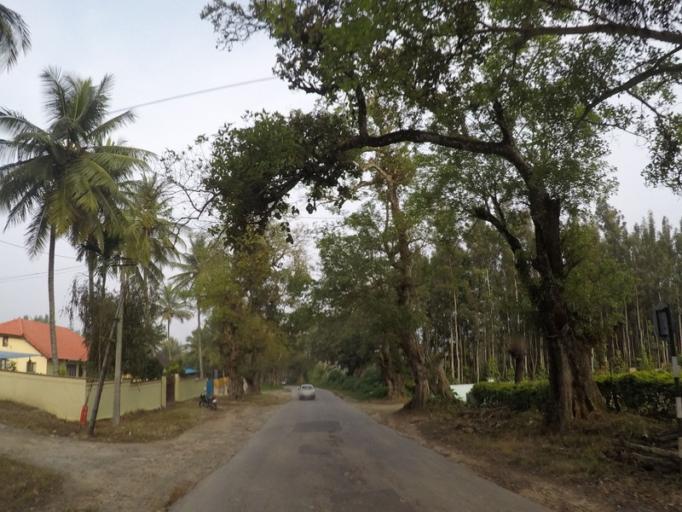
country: IN
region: Karnataka
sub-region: Chikmagalur
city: Chikmagalur
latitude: 13.2681
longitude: 75.7202
